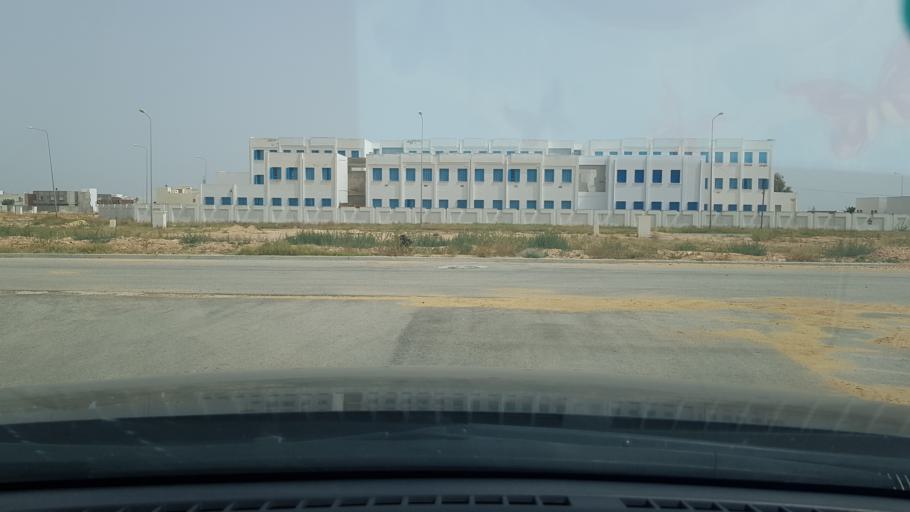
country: TN
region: Safaqis
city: Al Qarmadah
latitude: 34.8267
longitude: 10.7427
